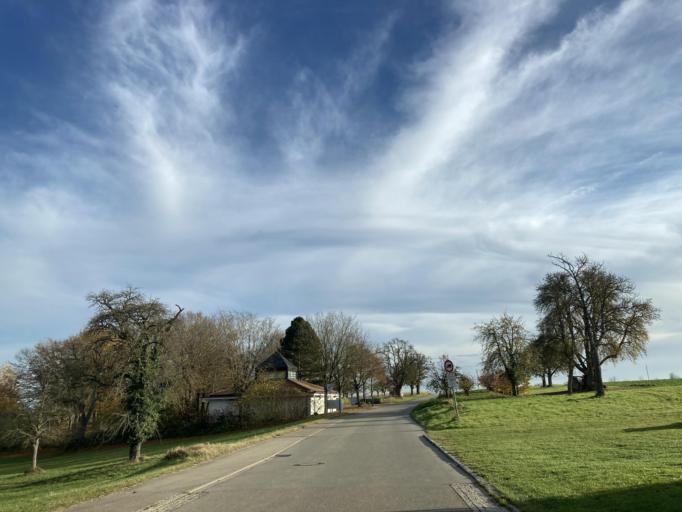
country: DE
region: Baden-Wuerttemberg
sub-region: Regierungsbezirk Stuttgart
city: Bondorf
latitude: 48.4711
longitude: 8.8213
